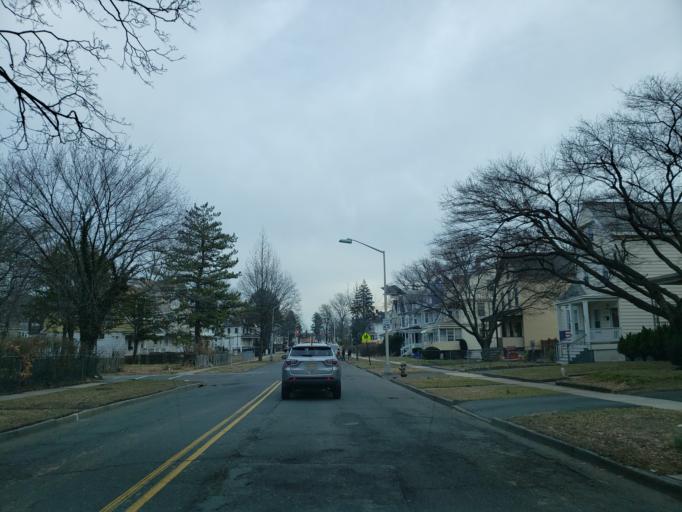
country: US
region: New Jersey
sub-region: Essex County
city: East Orange
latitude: 40.7778
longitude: -74.2166
